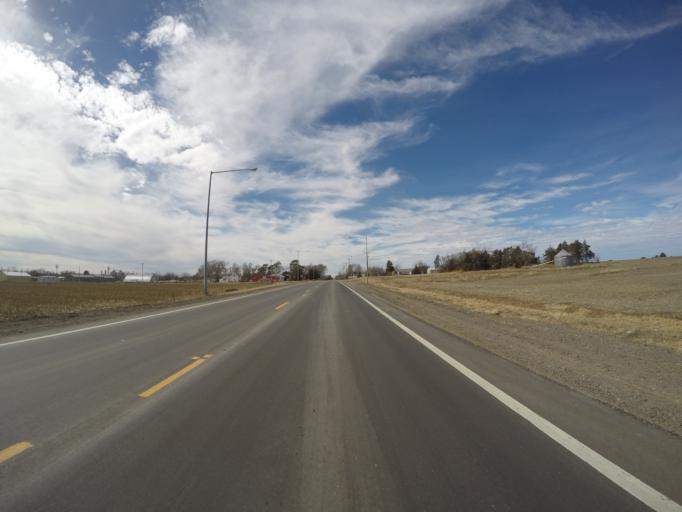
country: US
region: Nebraska
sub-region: Franklin County
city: Franklin
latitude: 40.0961
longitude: -98.9413
